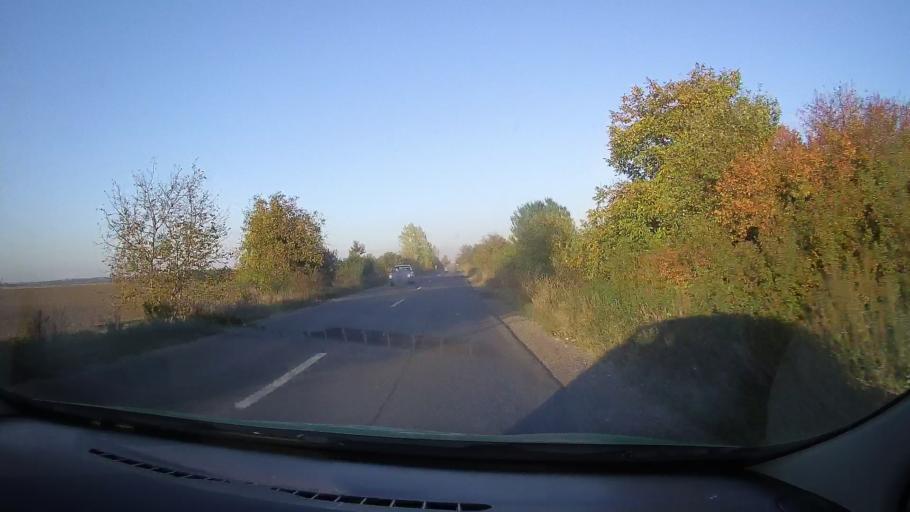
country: RO
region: Bihor
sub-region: Comuna Salard
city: Salard
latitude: 47.1949
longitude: 22.0004
